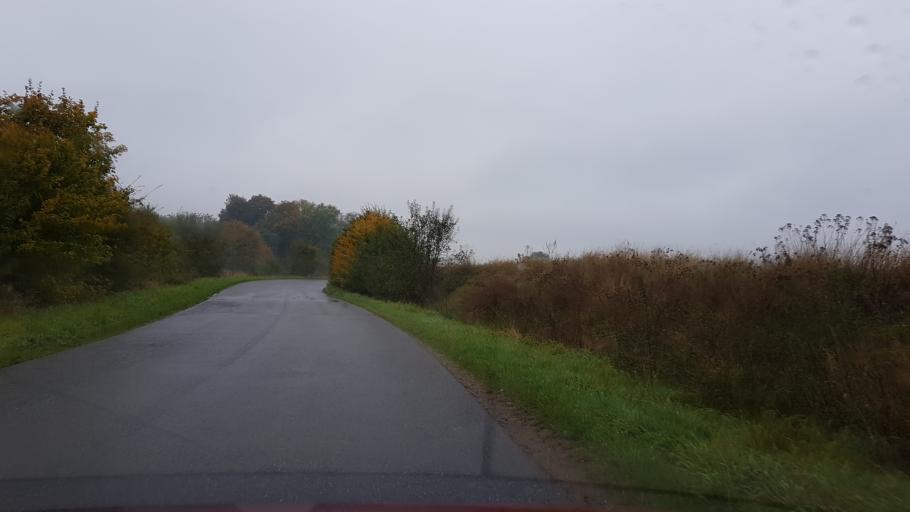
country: PL
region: Greater Poland Voivodeship
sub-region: Powiat zlotowski
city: Tarnowka
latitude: 53.3434
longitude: 16.9176
